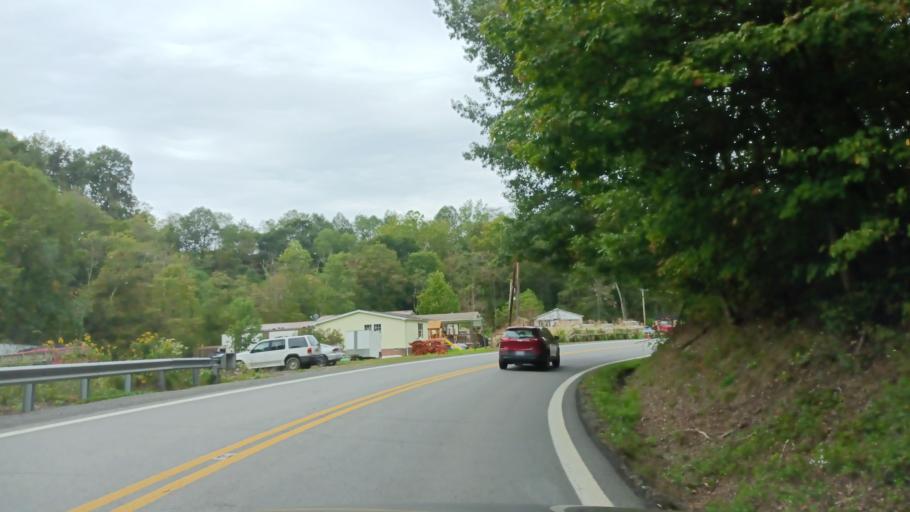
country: US
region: West Virginia
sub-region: Taylor County
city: Grafton
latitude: 39.3334
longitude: -79.8977
